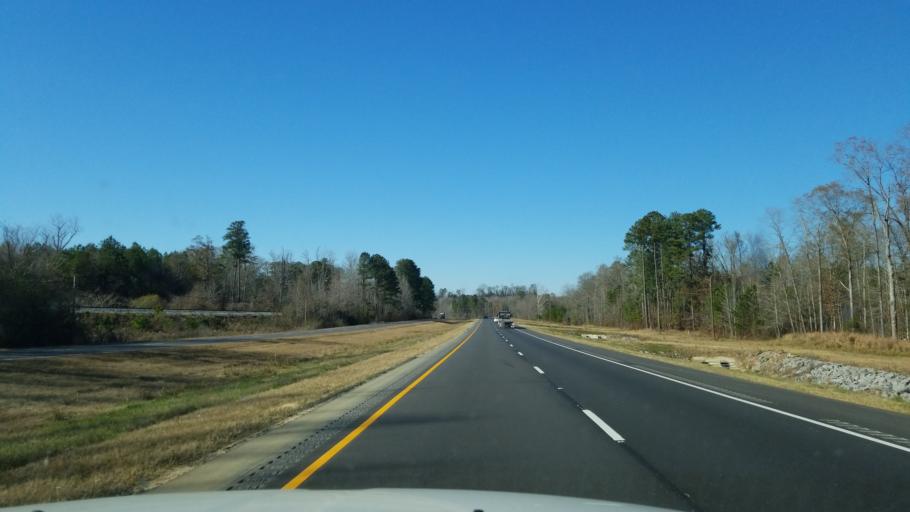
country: US
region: Alabama
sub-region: Pickens County
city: Reform
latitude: 33.3674
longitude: -87.9837
